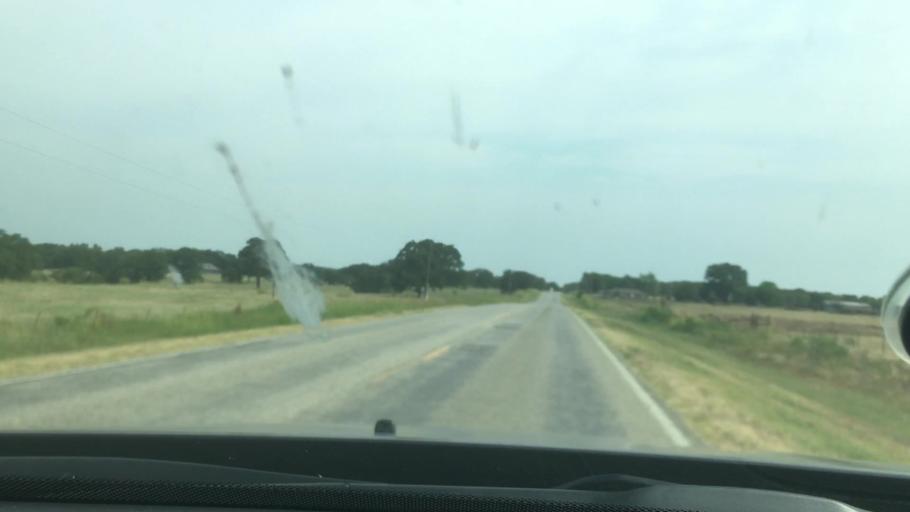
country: US
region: Oklahoma
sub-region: Johnston County
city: Tishomingo
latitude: 34.3133
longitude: -96.4247
